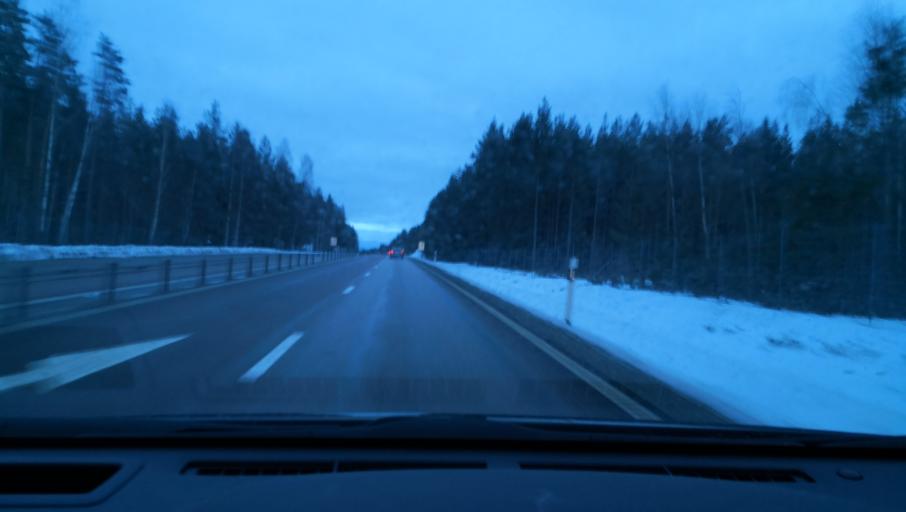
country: SE
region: Vaestmanland
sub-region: Surahammars Kommun
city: Ramnas
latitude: 59.8339
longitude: 16.0753
